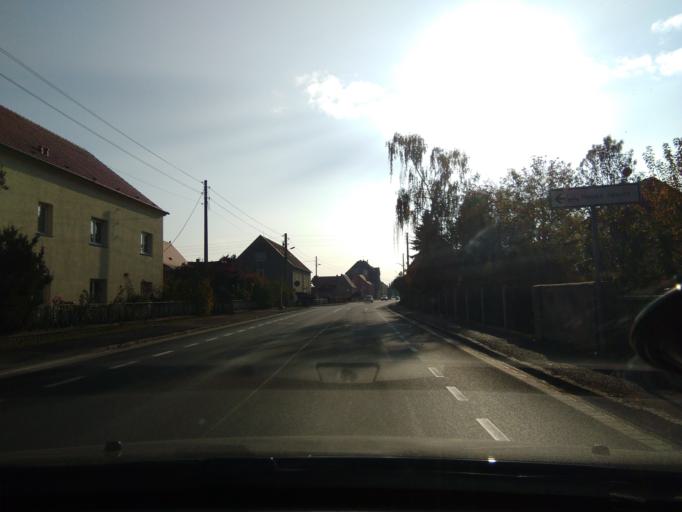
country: DE
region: Saxony
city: Weinbohla
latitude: 51.1337
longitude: 13.5382
